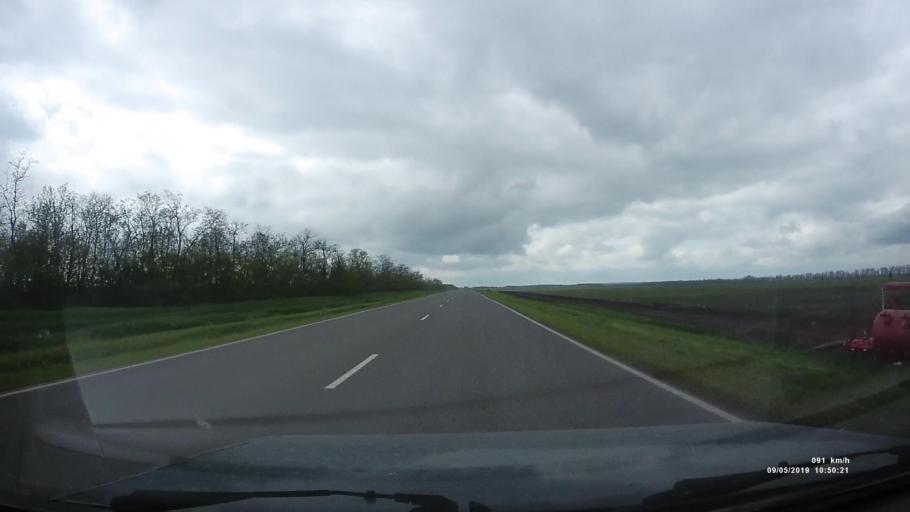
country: RU
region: Rostov
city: Peshkovo
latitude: 46.9298
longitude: 39.3553
